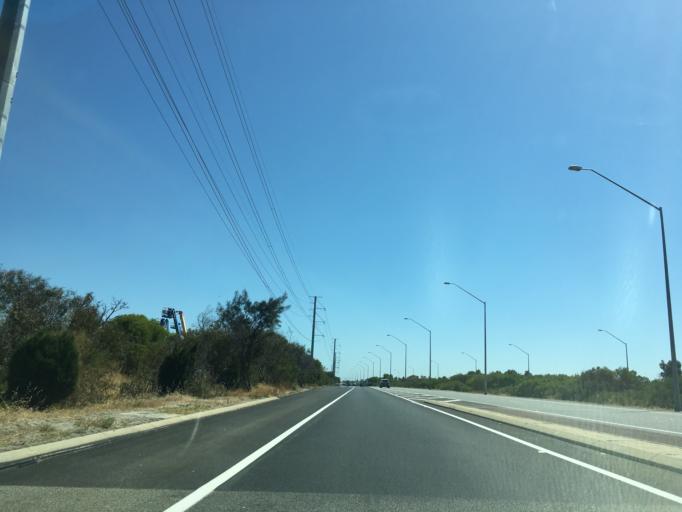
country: AU
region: Western Australia
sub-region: Canning
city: Canning Vale
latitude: -32.0588
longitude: 115.9031
